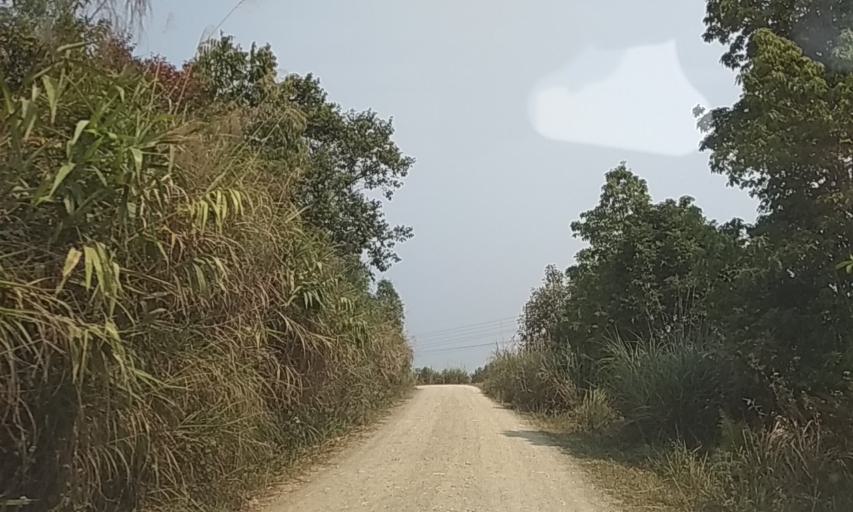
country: TH
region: Nan
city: Chaloem Phra Kiat
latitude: 20.0529
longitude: 101.0800
